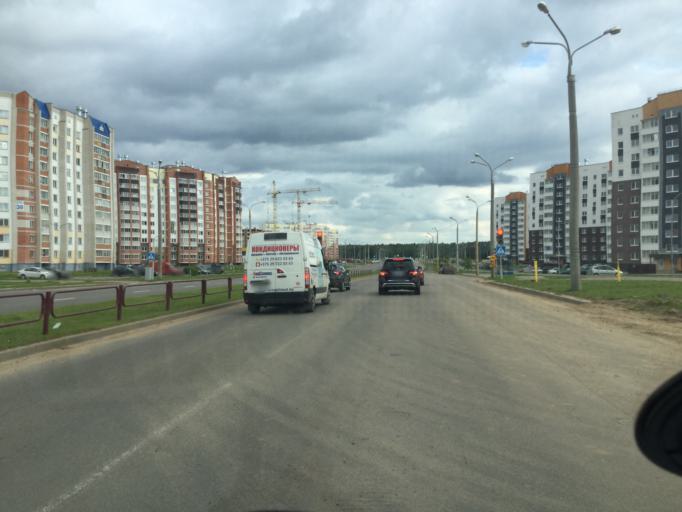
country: BY
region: Vitebsk
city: Vitebsk
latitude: 55.1645
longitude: 30.2701
